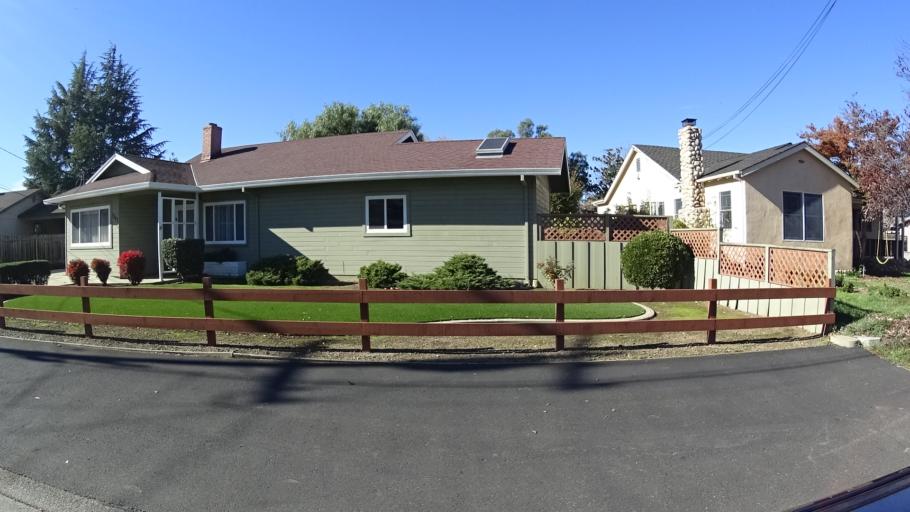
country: US
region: California
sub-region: Santa Clara County
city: Sunnyvale
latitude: 37.3506
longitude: -122.0101
